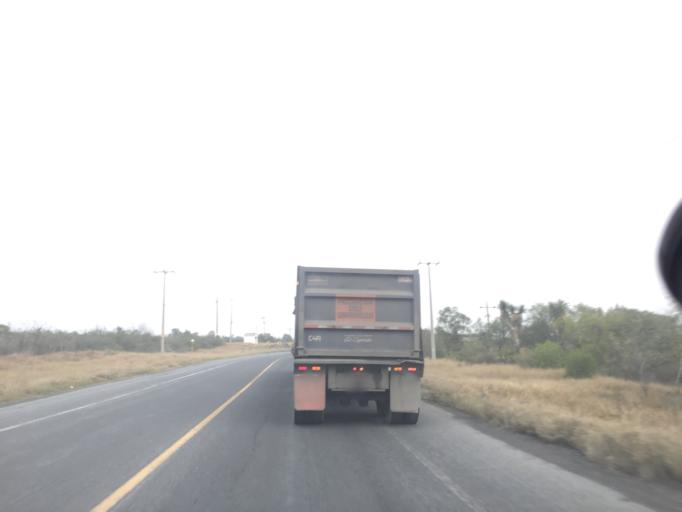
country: MX
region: Nuevo Leon
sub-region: Salinas Victoria
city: Las Torres
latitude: 25.9501
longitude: -100.4190
